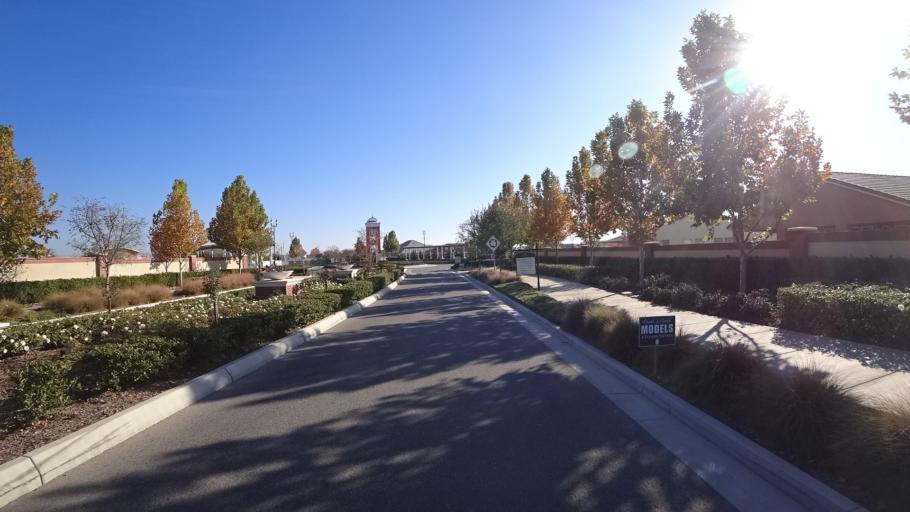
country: US
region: California
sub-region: Kern County
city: Rosedale
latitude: 35.3389
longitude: -119.1514
